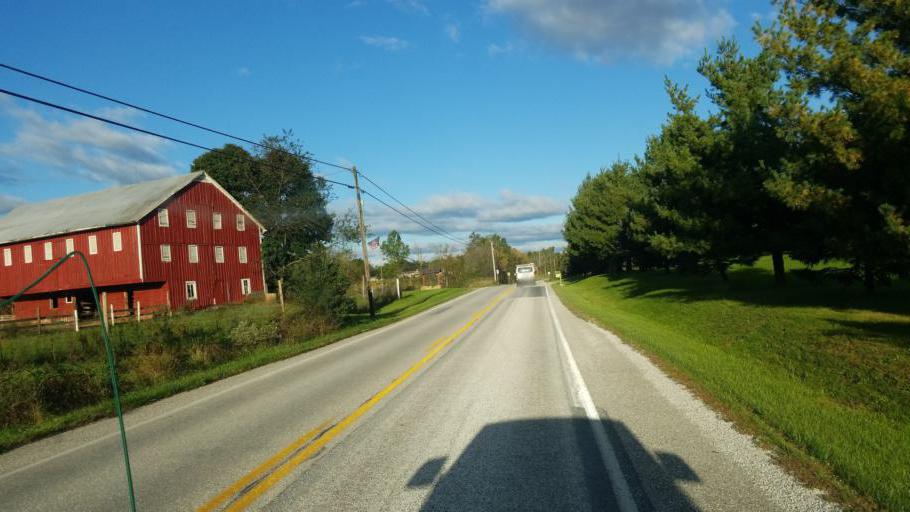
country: US
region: Pennsylvania
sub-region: Adams County
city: Biglerville
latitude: 39.8943
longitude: -77.1951
